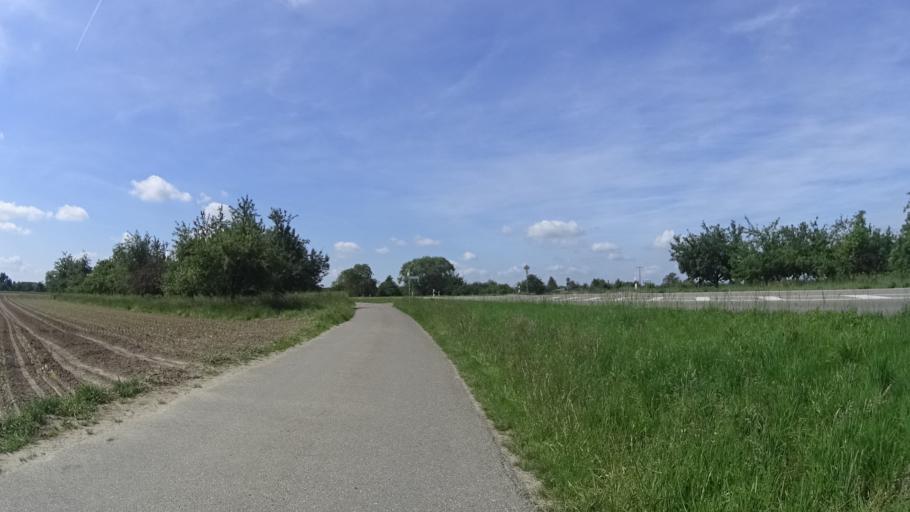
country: DE
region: Baden-Wuerttemberg
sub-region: Freiburg Region
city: Meissenheim
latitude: 48.4735
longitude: 7.8123
